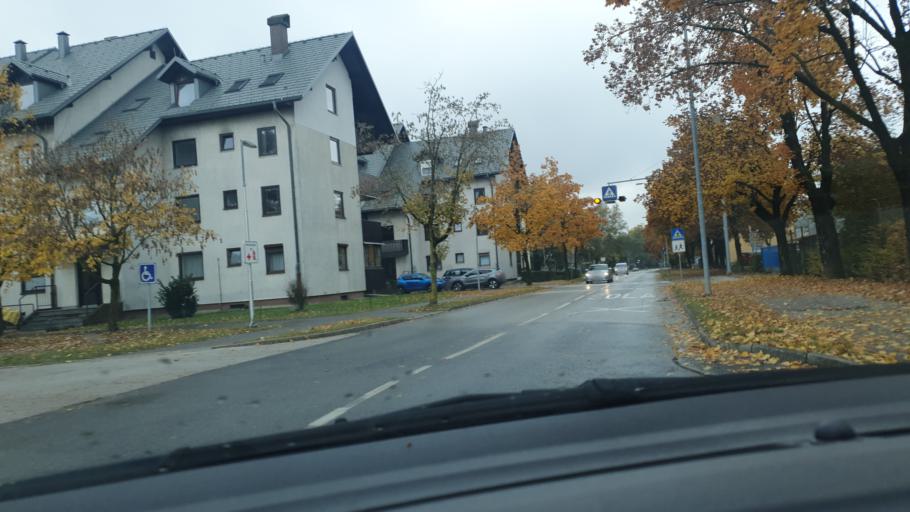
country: SI
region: Kranj
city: Kranj
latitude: 46.2347
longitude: 14.3669
